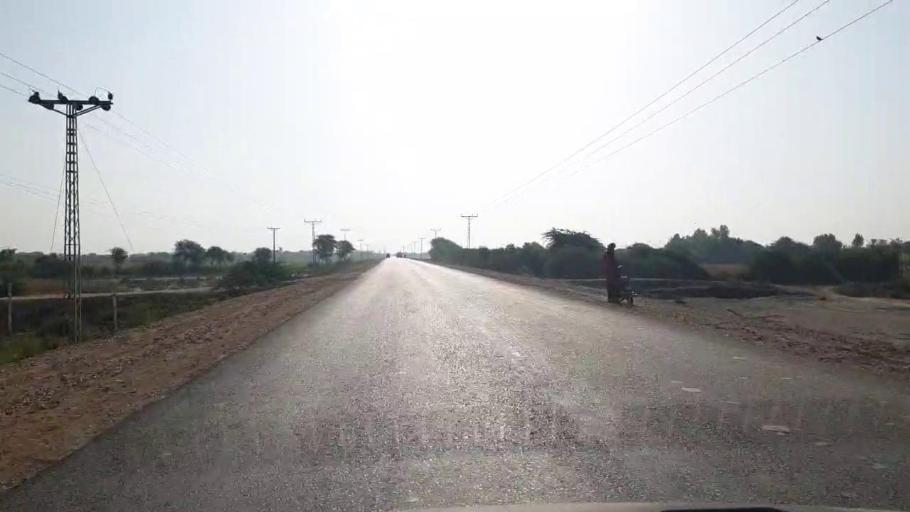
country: PK
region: Sindh
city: Badin
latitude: 24.6712
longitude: 68.8584
